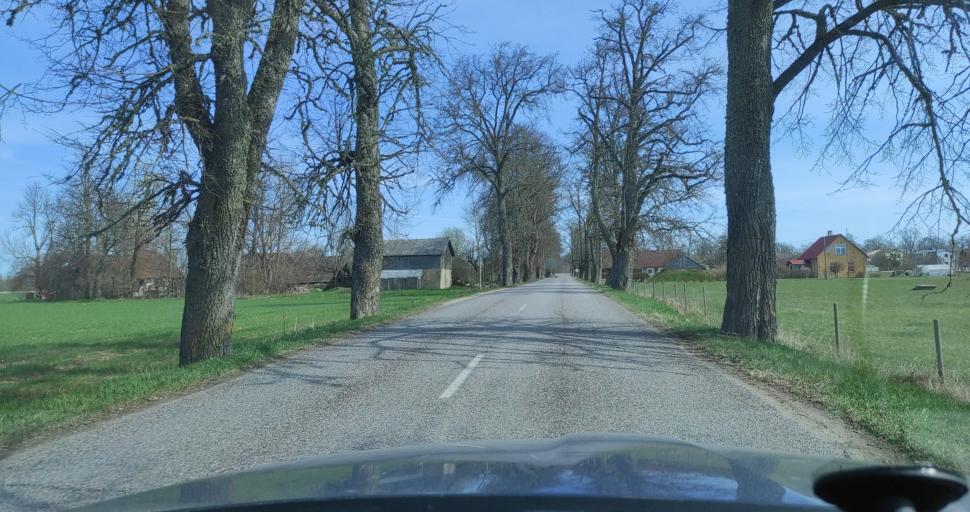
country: LV
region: Talsu Rajons
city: Stende
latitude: 57.2210
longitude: 22.5090
